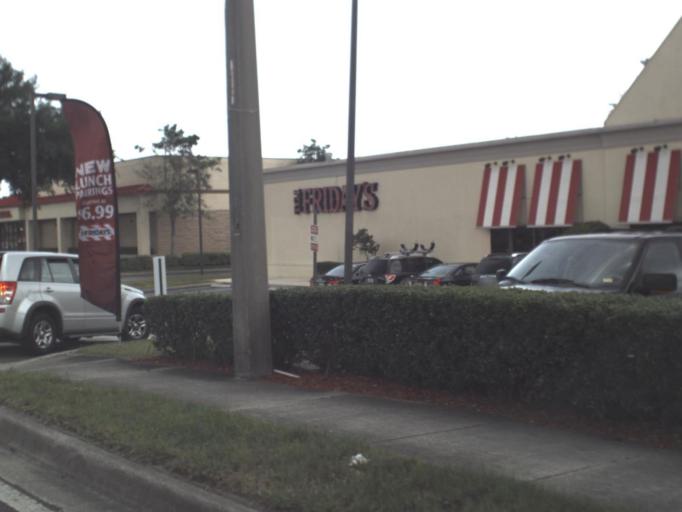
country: US
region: Florida
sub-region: Duval County
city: Jacksonville
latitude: 30.3193
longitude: -81.5538
